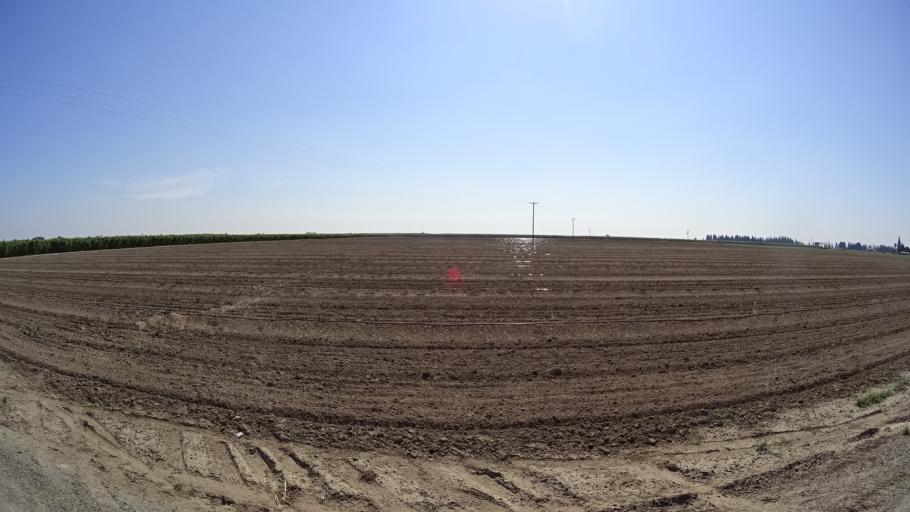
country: US
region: California
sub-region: Kings County
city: Lucerne
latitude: 36.4223
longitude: -119.5828
